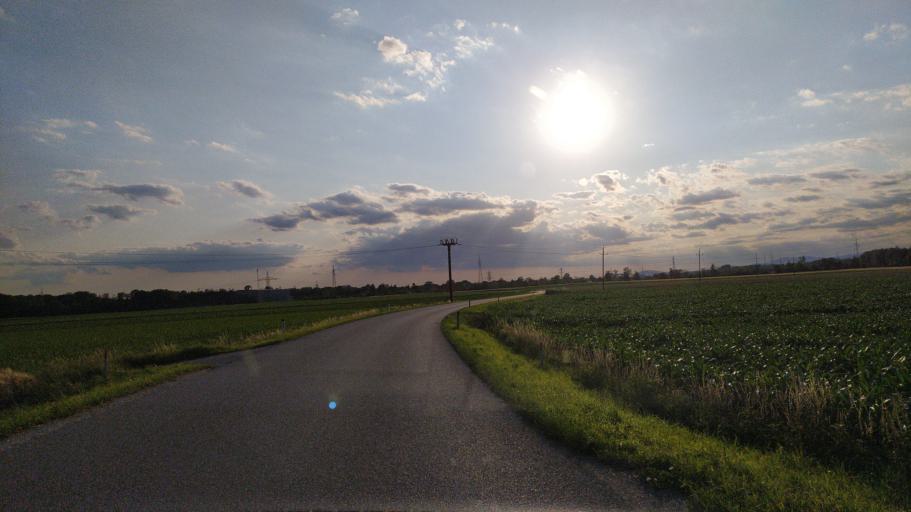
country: AT
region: Lower Austria
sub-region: Politischer Bezirk Amstetten
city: Ennsdorf
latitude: 48.2258
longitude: 14.5417
